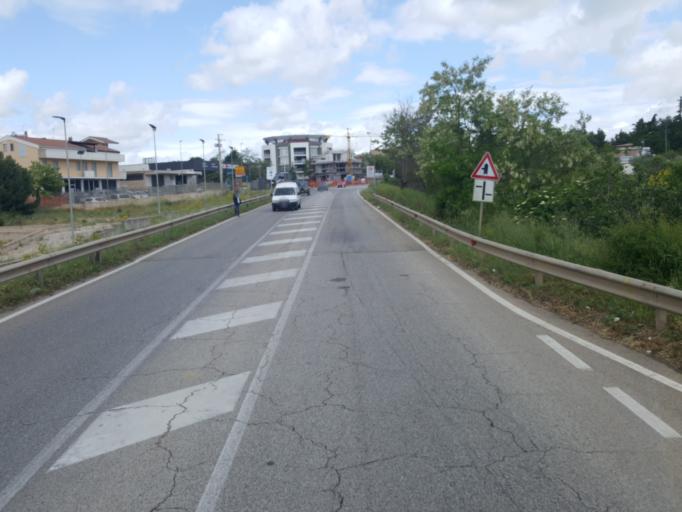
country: IT
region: Apulia
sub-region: Provincia di Bari
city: Altamura
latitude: 40.8120
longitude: 16.5548
